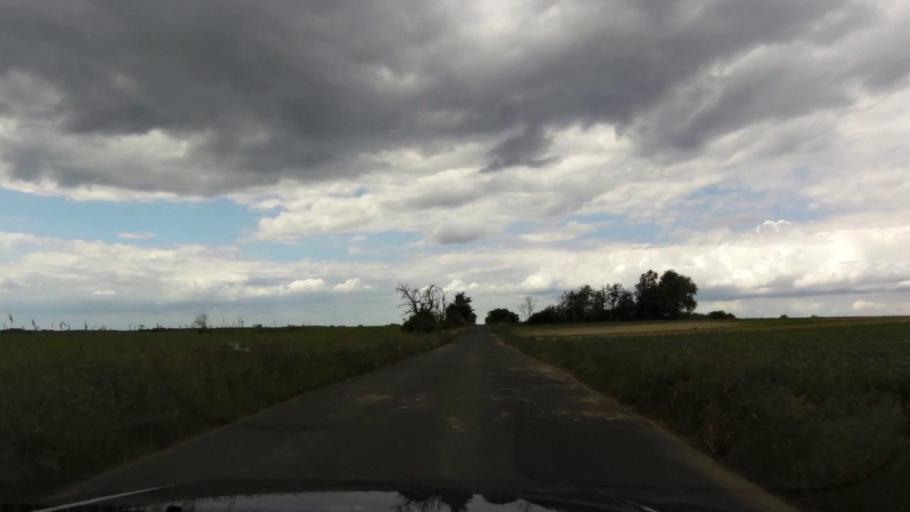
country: PL
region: West Pomeranian Voivodeship
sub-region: Powiat mysliborski
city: Mysliborz
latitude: 52.9788
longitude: 14.7867
